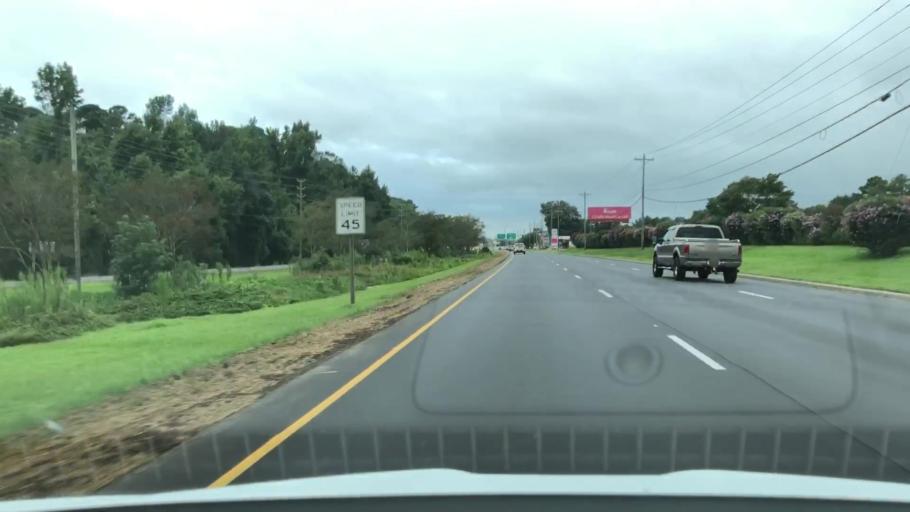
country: US
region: North Carolina
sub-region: Lenoir County
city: Kinston
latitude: 35.2659
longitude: -77.6347
